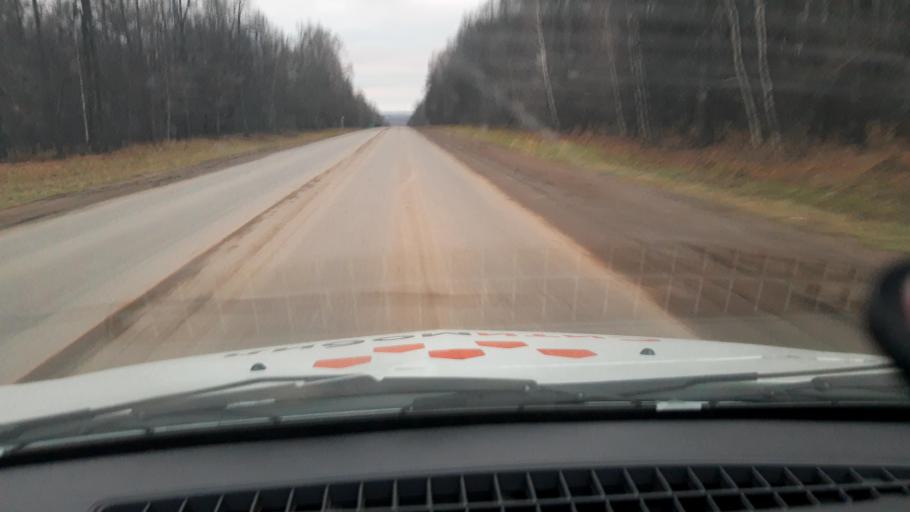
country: RU
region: Bashkortostan
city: Iglino
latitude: 54.7749
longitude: 56.4154
